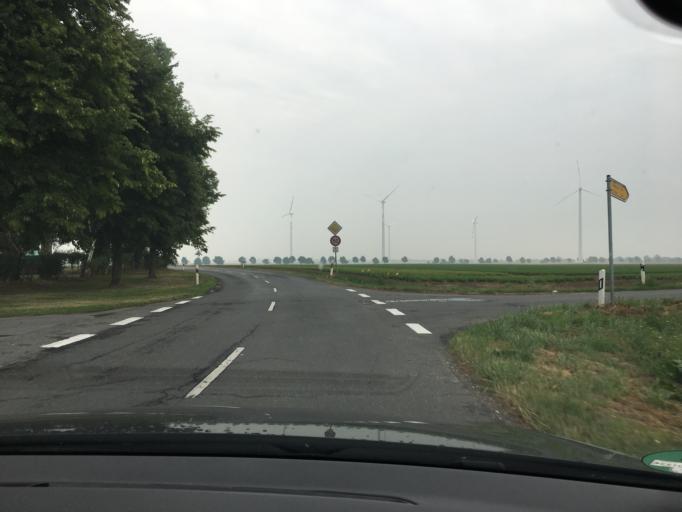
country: DE
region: North Rhine-Westphalia
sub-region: Regierungsbezirk Koln
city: Titz
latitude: 50.9603
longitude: 6.4114
